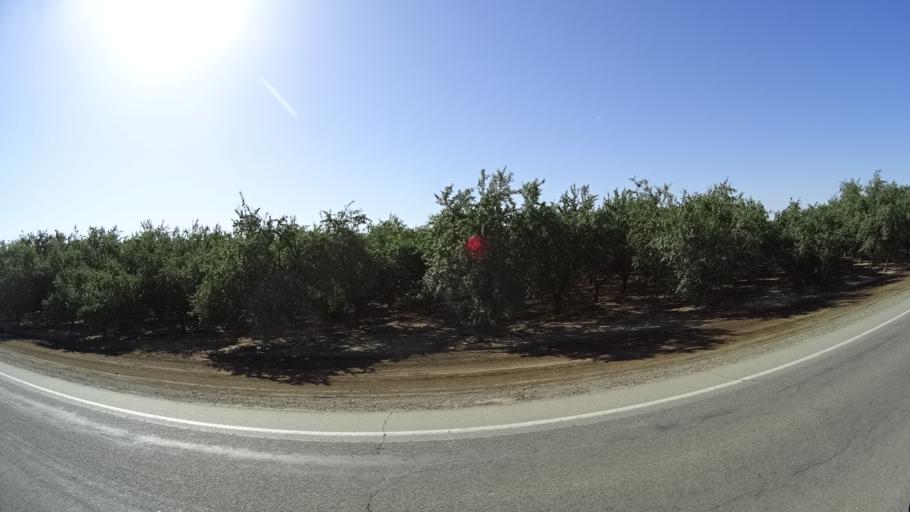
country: US
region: California
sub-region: Fresno County
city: Huron
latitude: 36.1053
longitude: -120.0528
